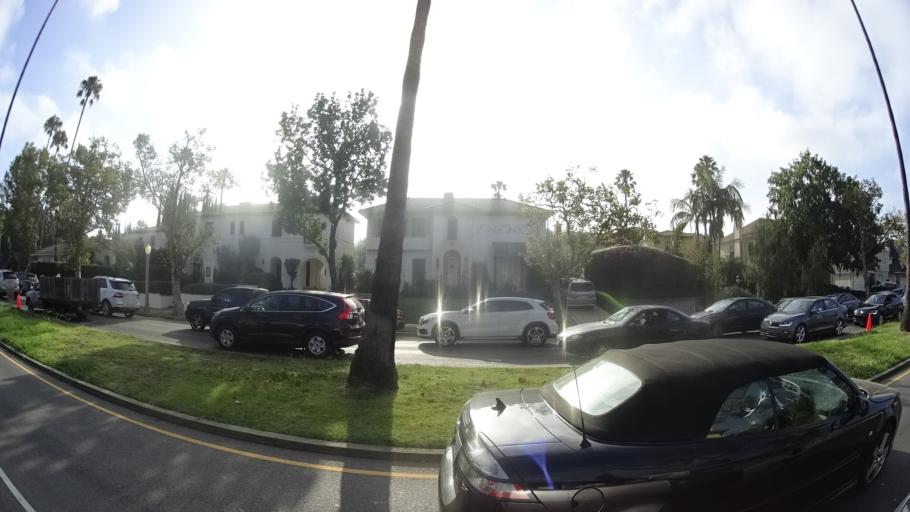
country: US
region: California
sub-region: Los Angeles County
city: Hollywood
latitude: 34.0756
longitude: -118.3387
